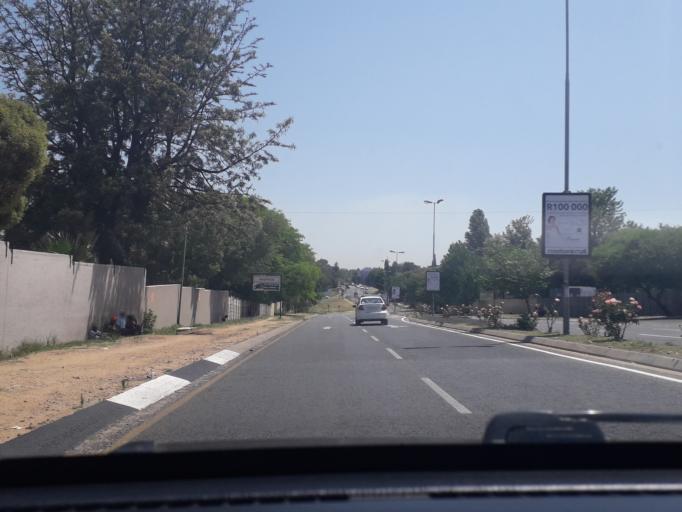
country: ZA
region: Gauteng
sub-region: City of Johannesburg Metropolitan Municipality
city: Modderfontein
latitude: -26.0873
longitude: 28.0794
